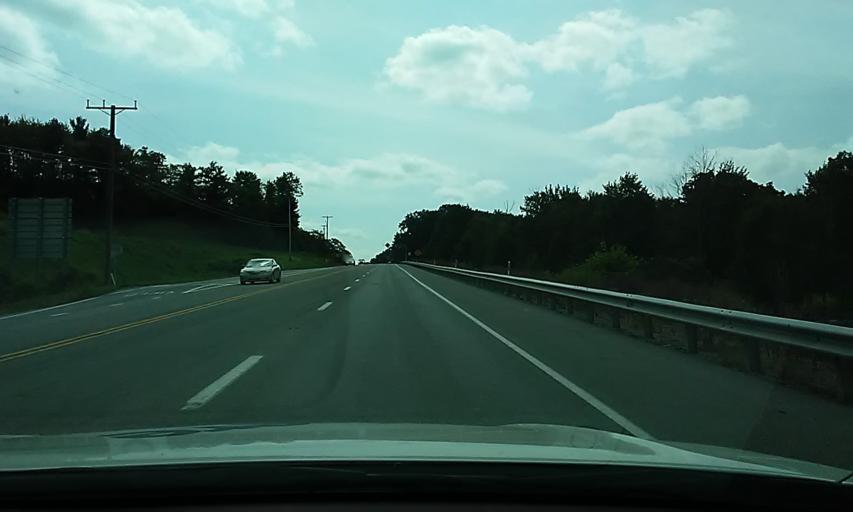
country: US
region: Pennsylvania
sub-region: Jefferson County
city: Punxsutawney
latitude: 40.9323
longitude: -78.9804
